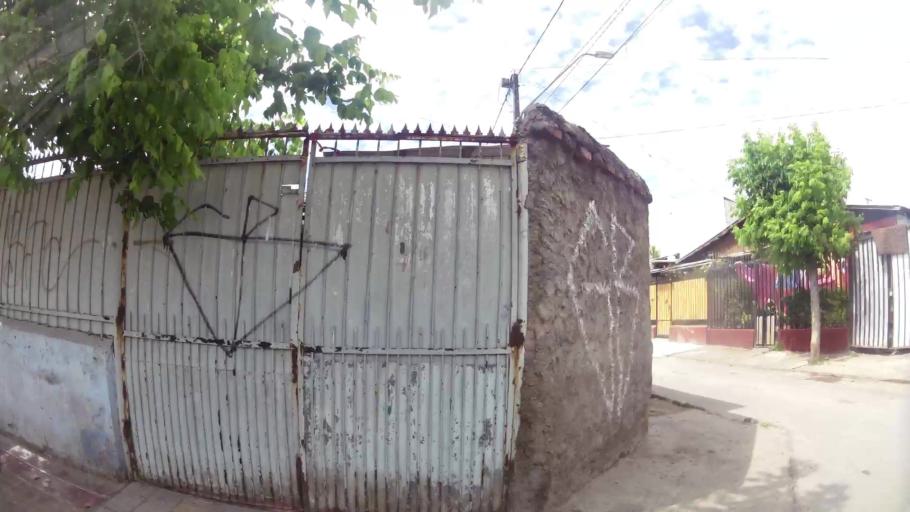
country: CL
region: Santiago Metropolitan
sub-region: Provincia de Santiago
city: La Pintana
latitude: -33.5867
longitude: -70.6643
